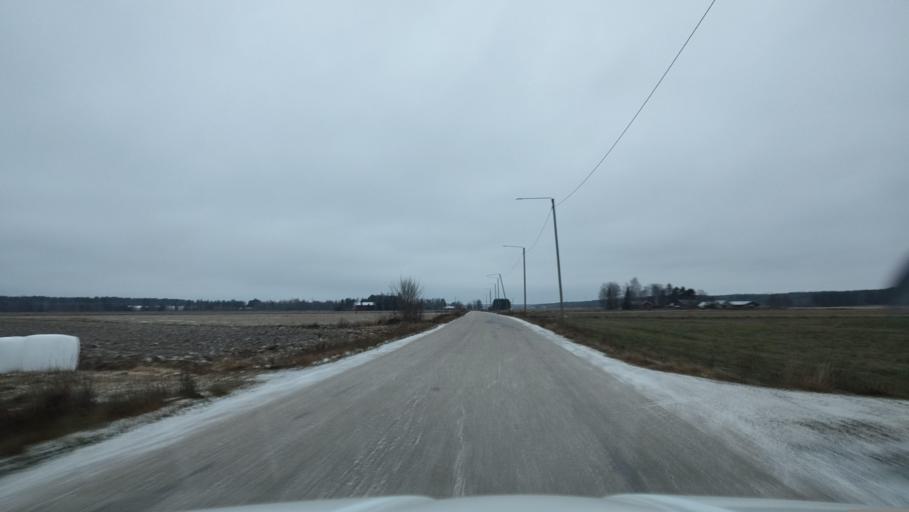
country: FI
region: Southern Ostrobothnia
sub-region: Suupohja
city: Karijoki
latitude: 62.2643
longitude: 21.6843
